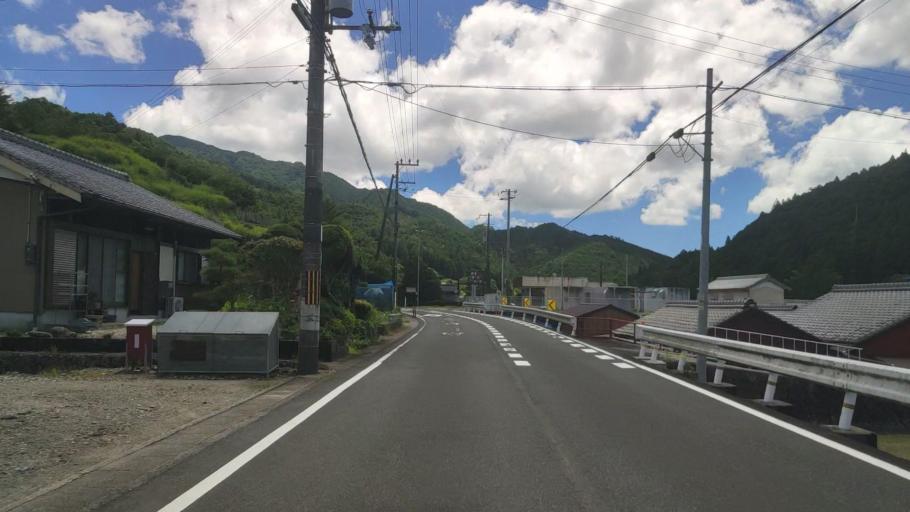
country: JP
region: Mie
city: Owase
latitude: 33.9755
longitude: 136.0556
